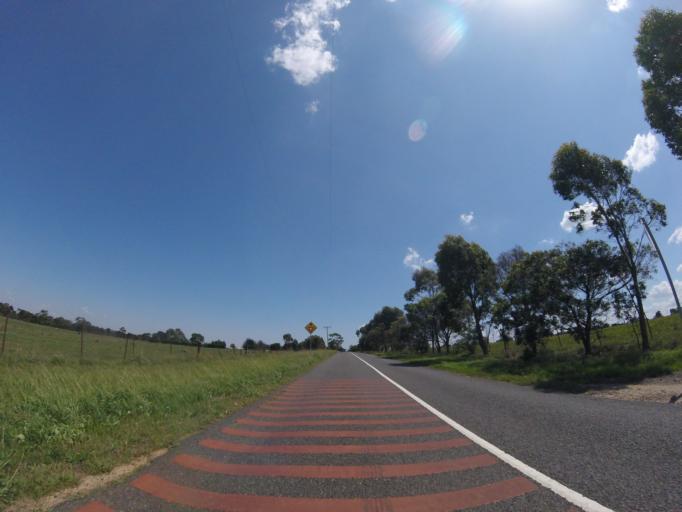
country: AU
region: Victoria
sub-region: Hume
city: Sunbury
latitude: -37.5730
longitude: 144.7929
